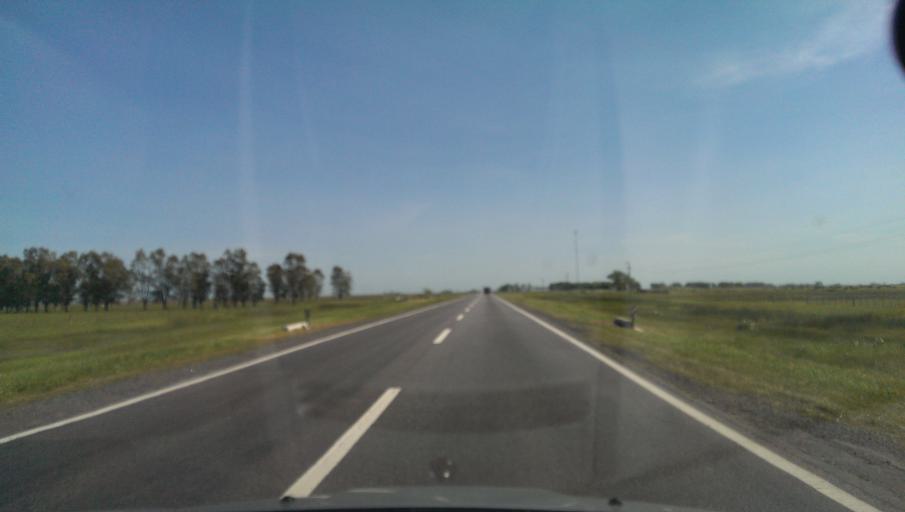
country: AR
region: Buenos Aires
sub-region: Partido de Azul
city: Azul
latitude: -36.6010
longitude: -59.6660
